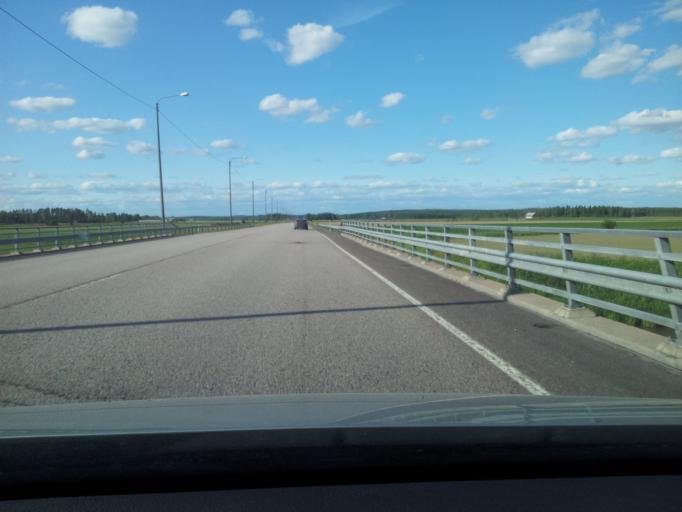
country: FI
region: Uusimaa
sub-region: Loviisa
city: Lapinjaervi
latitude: 60.6467
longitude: 26.2343
